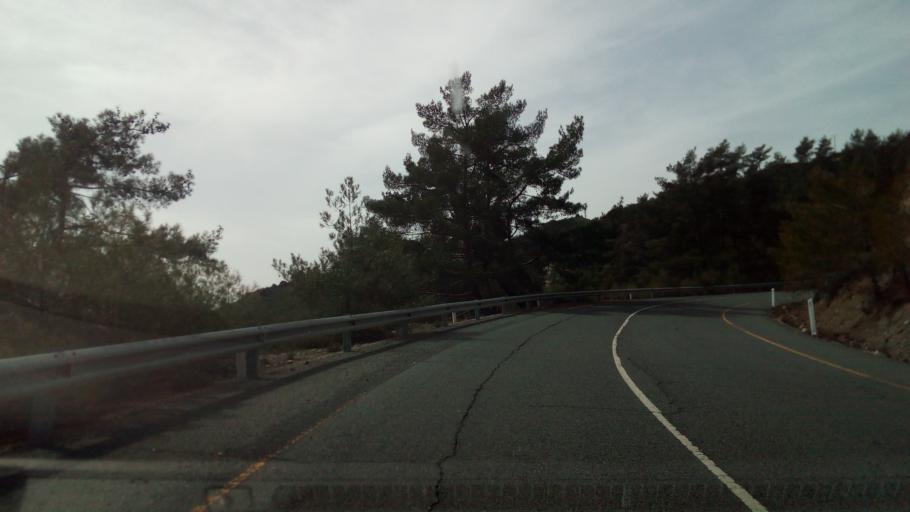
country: CY
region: Limassol
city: Pelendri
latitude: 34.8852
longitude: 32.9498
